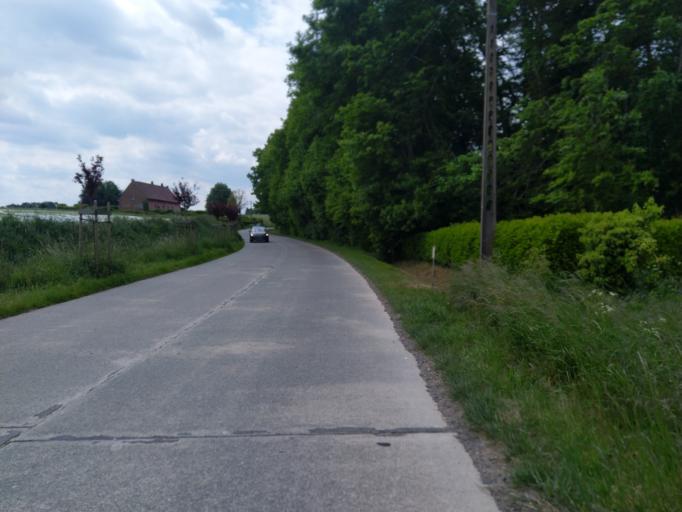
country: BE
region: Wallonia
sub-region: Province du Hainaut
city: Silly
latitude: 50.6142
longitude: 3.9611
